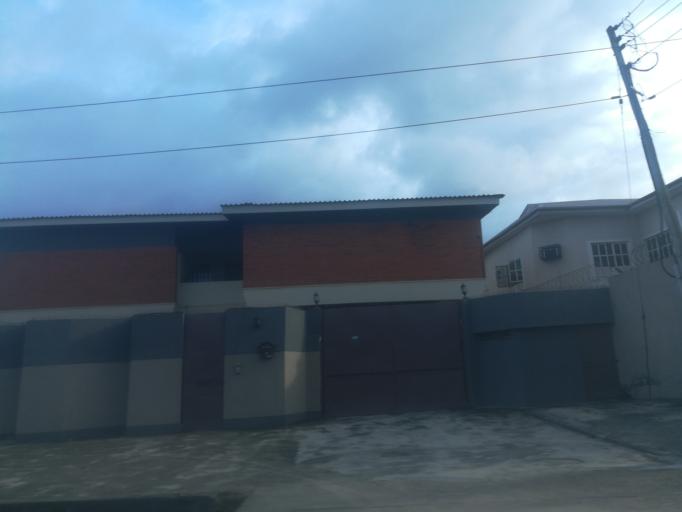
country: NG
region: Lagos
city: Somolu
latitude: 6.5470
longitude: 3.3888
